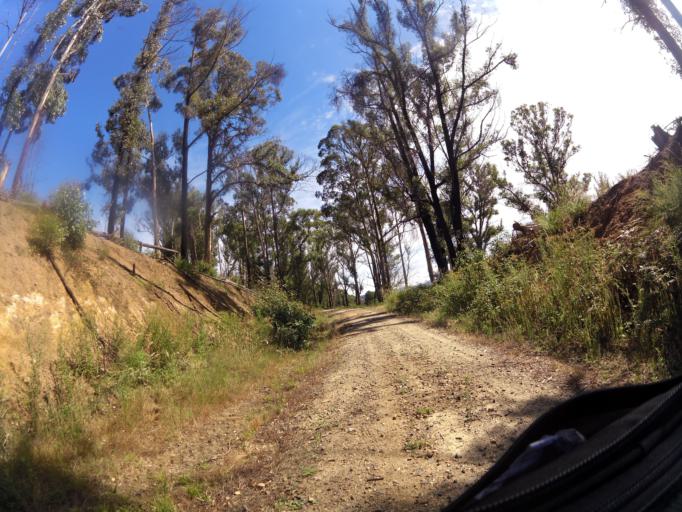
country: AU
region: Victoria
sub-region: East Gippsland
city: Lakes Entrance
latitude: -37.7297
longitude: 148.1629
